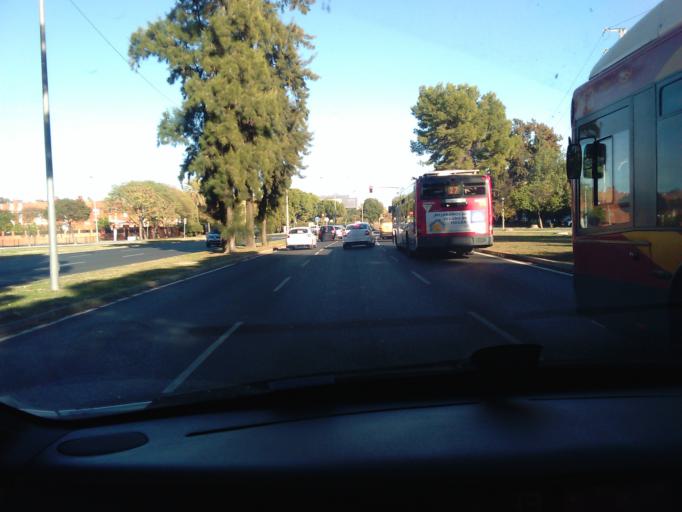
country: ES
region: Andalusia
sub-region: Provincia de Sevilla
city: Sevilla
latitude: 37.4032
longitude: -5.9404
